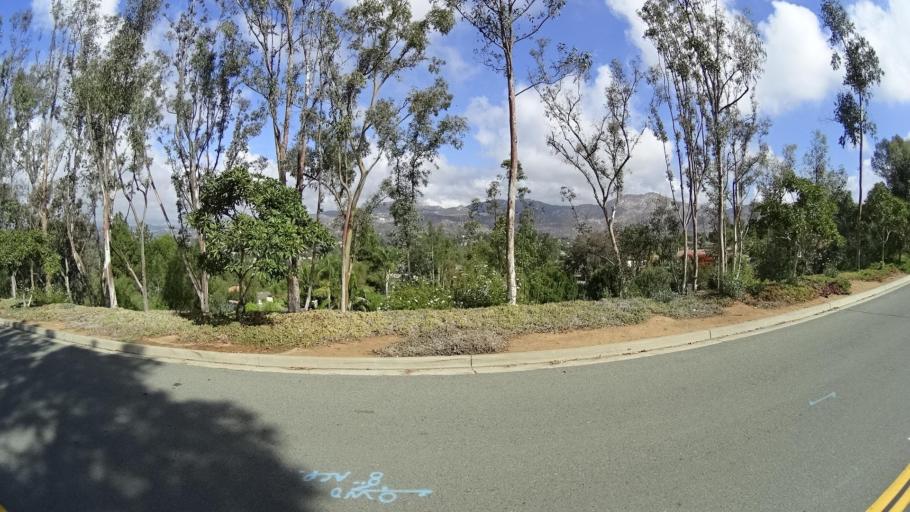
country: US
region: California
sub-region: San Diego County
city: Granite Hills
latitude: 32.7770
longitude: -116.9038
